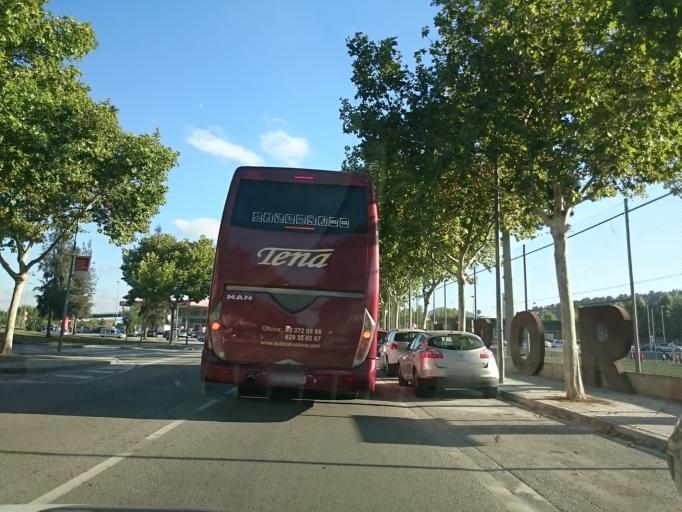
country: ES
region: Catalonia
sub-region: Provincia de Barcelona
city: Palleja
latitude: 41.4202
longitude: 2.0009
